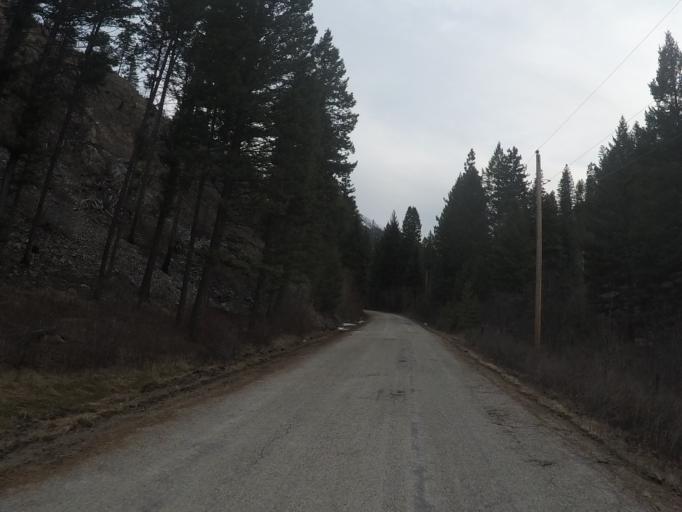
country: US
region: Montana
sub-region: Ravalli County
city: Hamilton
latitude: 45.8496
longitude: -114.0331
